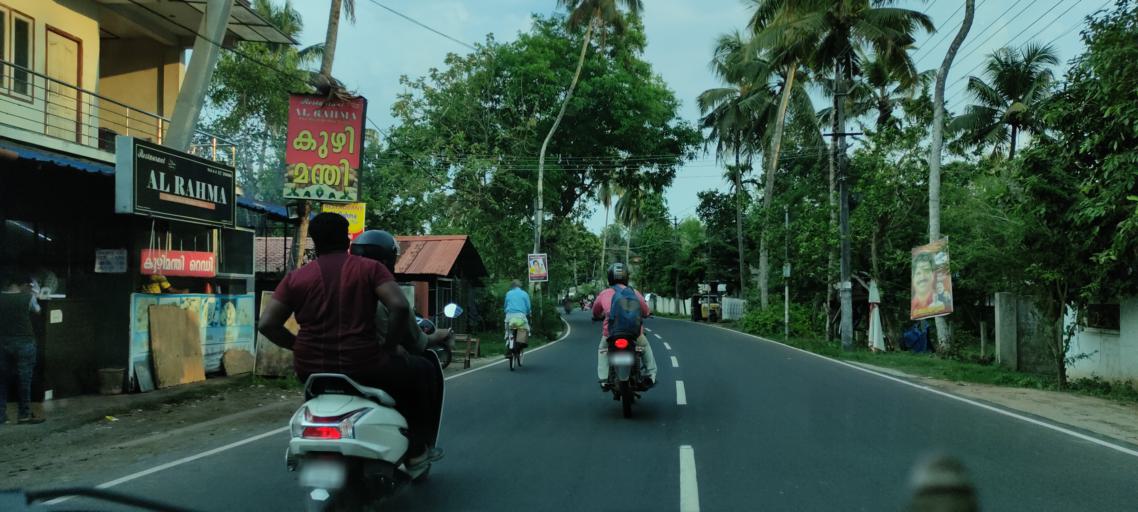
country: IN
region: Kerala
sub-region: Alappuzha
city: Arukutti
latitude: 9.8587
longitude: 76.3249
